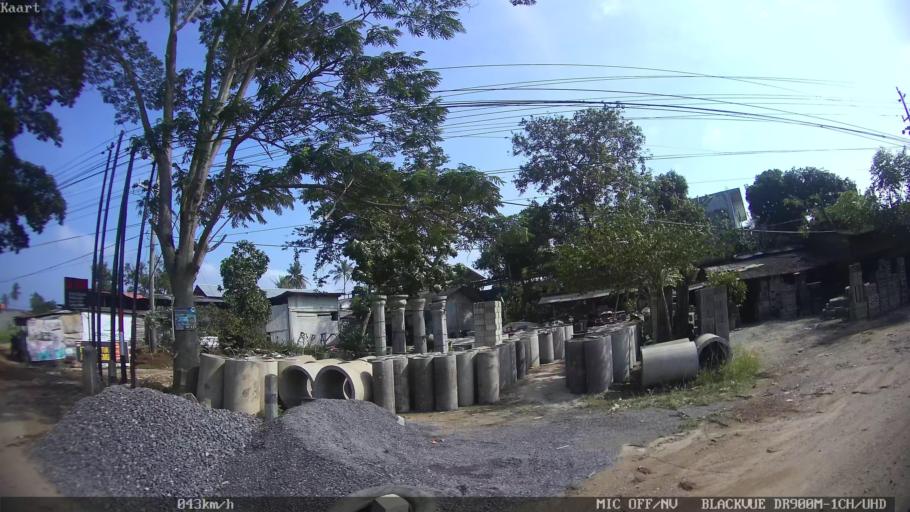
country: ID
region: Lampung
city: Kedaton
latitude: -5.3577
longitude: 105.2479
